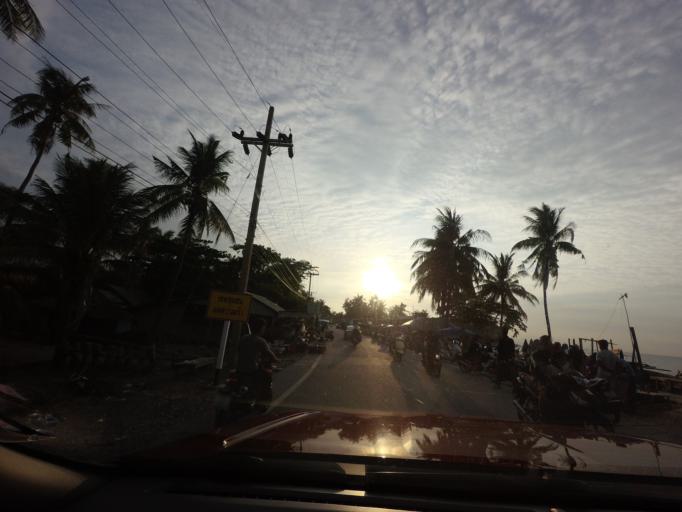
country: TH
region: Pattani
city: Yaring
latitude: 6.9286
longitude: 101.3244
